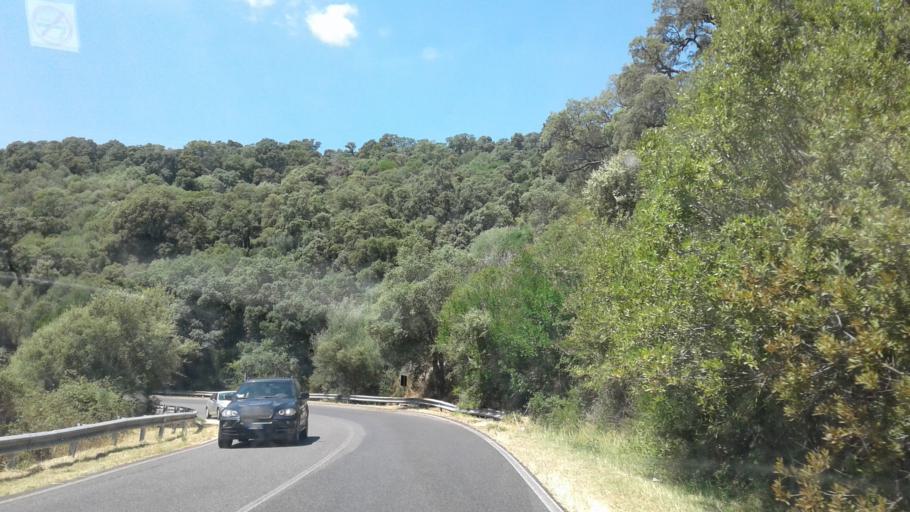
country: IT
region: Sardinia
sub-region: Provincia di Olbia-Tempio
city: Luras
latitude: 40.9448
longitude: 9.1933
